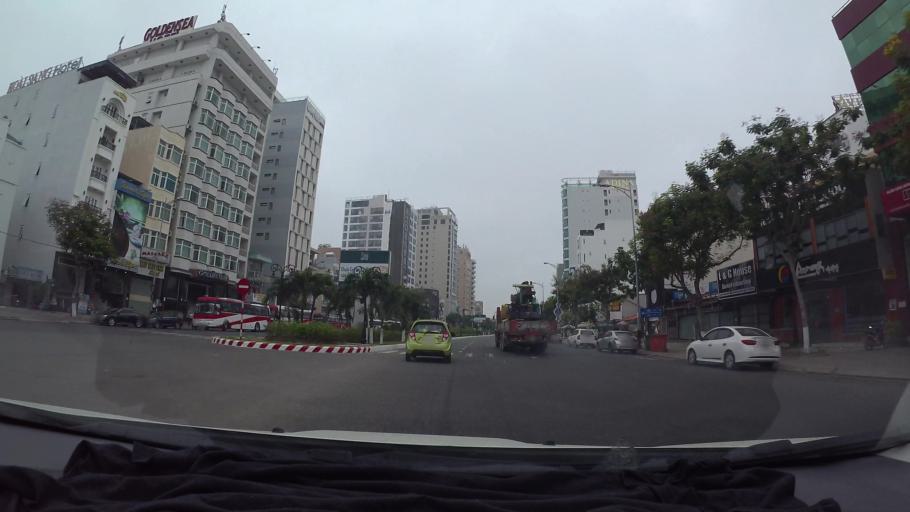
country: VN
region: Da Nang
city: Son Tra
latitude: 16.0704
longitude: 108.2378
